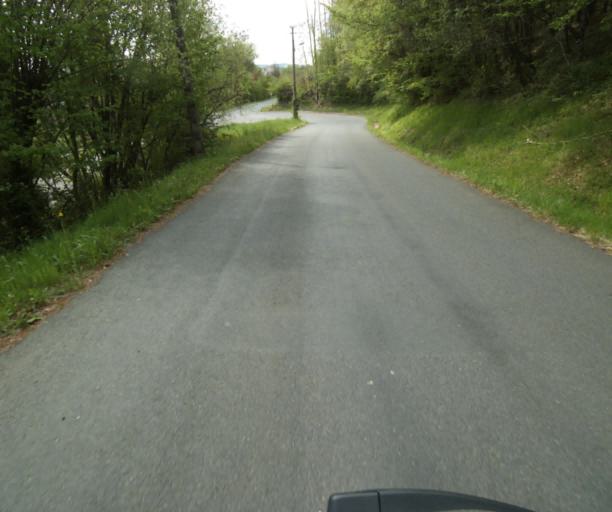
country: FR
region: Limousin
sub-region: Departement de la Correze
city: Tulle
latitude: 45.2835
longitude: 1.7669
